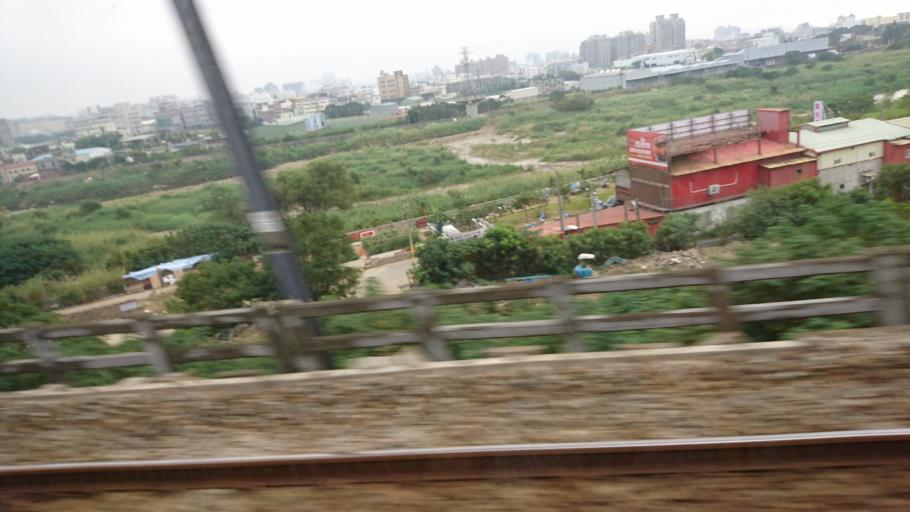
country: TW
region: Taiwan
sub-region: Hsinchu
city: Zhubei
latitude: 24.8545
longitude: 121.0099
